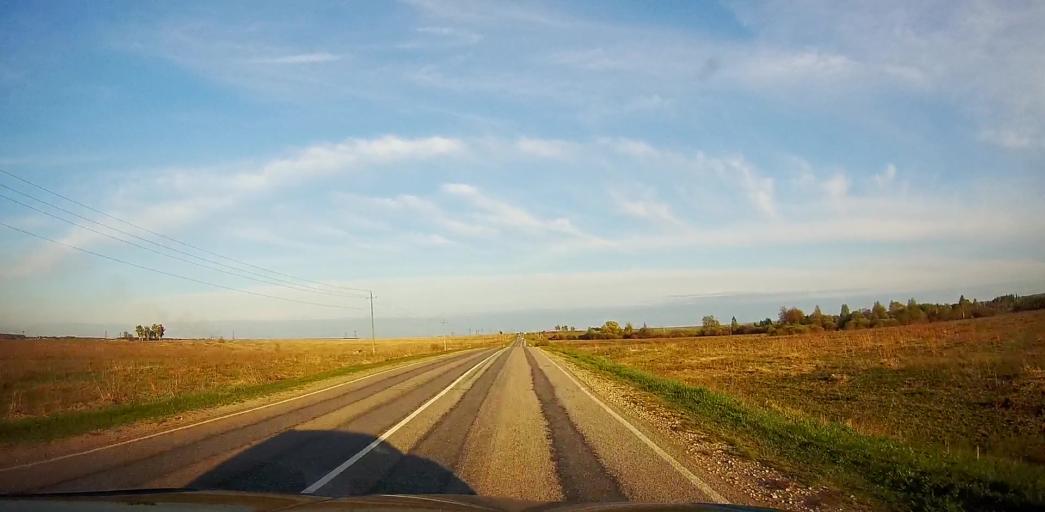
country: RU
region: Moskovskaya
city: Meshcherino
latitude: 55.2726
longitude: 38.2342
